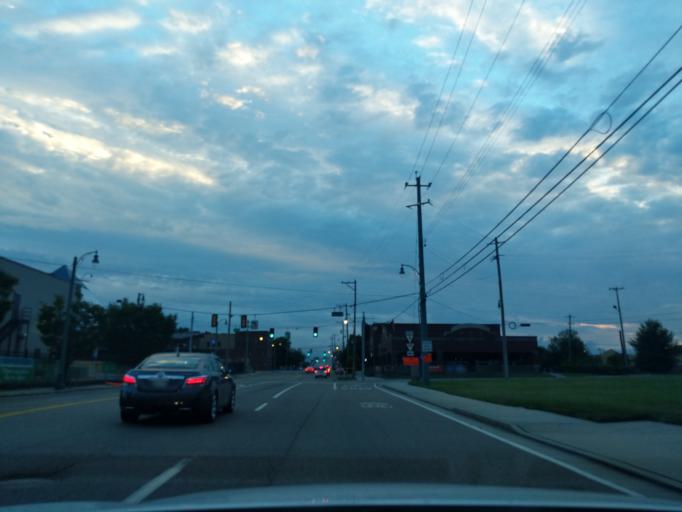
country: US
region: Tennessee
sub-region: Shelby County
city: Memphis
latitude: 35.1567
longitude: -90.0458
